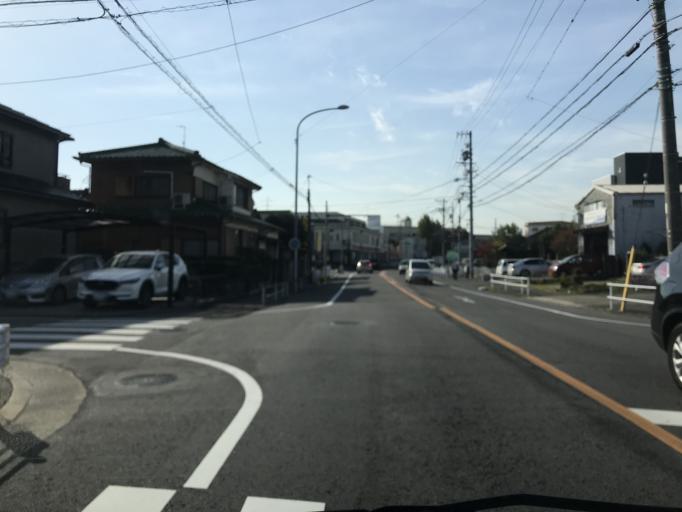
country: JP
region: Aichi
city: Nagoya-shi
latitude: 35.2002
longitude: 136.8665
